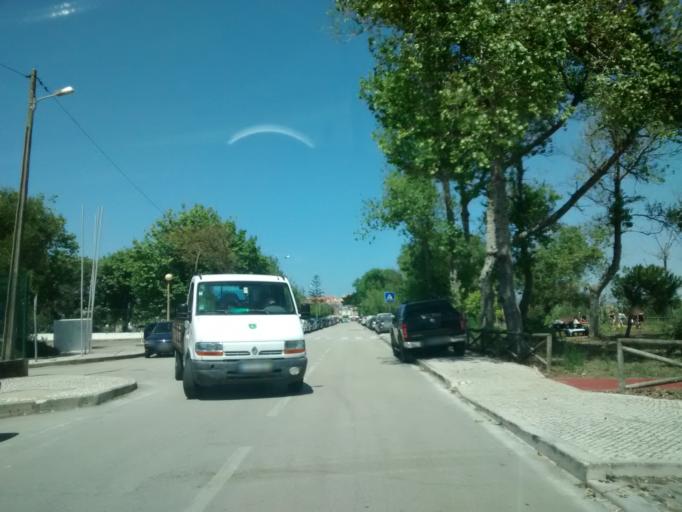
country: PT
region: Coimbra
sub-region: Mira
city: Mira
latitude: 40.4488
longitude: -8.8007
